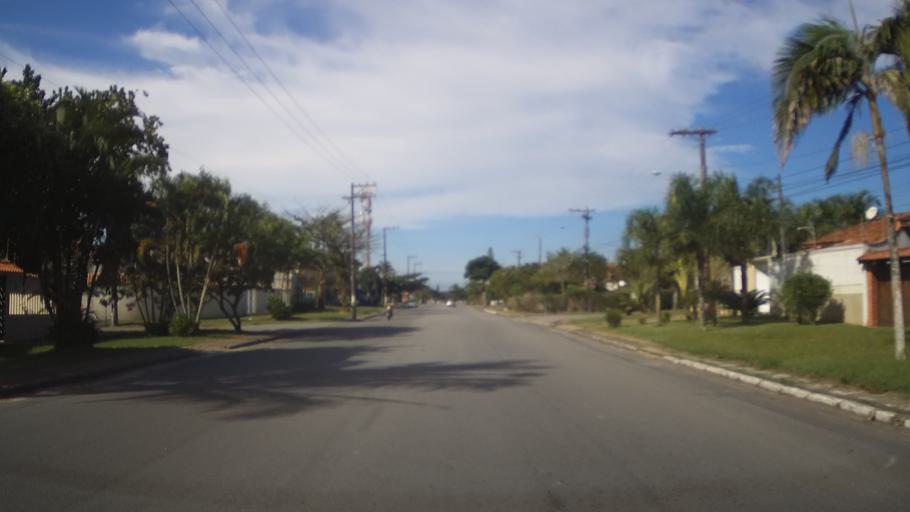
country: BR
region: Sao Paulo
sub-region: Itanhaem
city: Itanhaem
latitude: -24.1738
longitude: -46.7692
